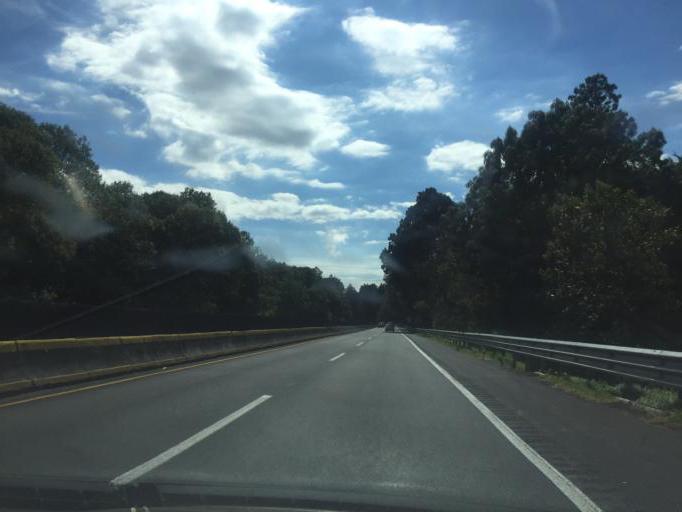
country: MX
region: Morelos
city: Tres Marias
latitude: 19.0349
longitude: -99.2267
